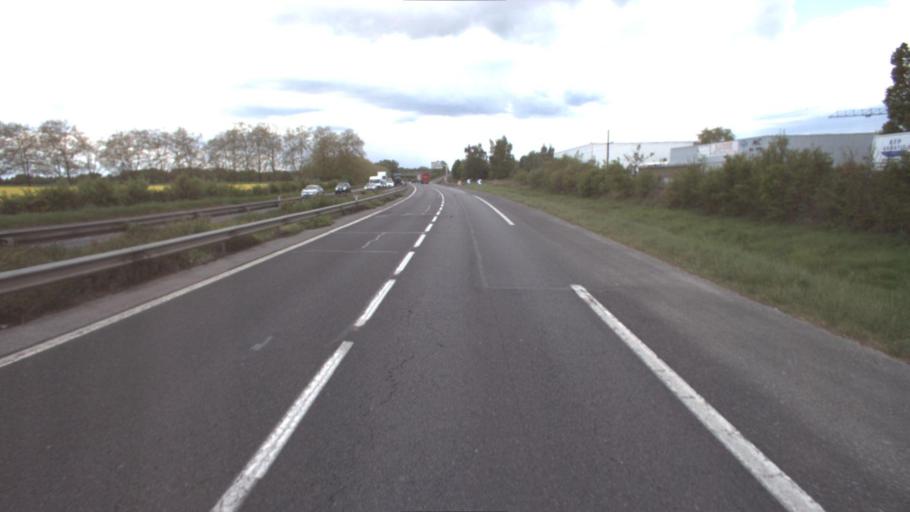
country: FR
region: Ile-de-France
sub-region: Departement de Seine-et-Marne
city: Tournan-en-Brie
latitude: 48.7331
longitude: 2.7846
